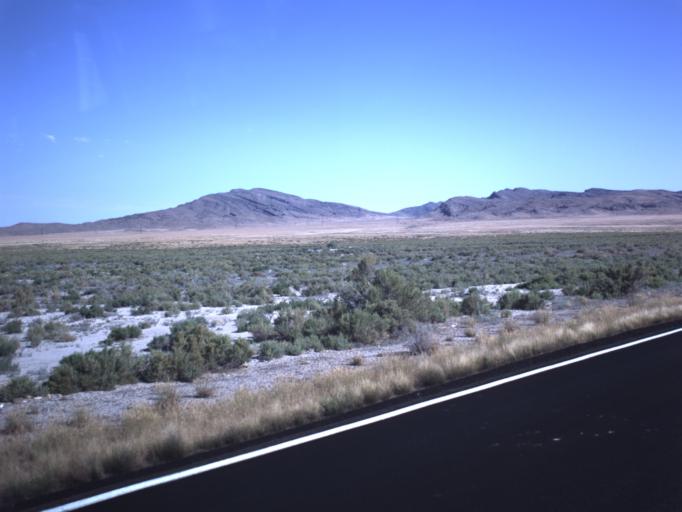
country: US
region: Utah
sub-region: Beaver County
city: Milford
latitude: 38.7243
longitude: -112.9677
